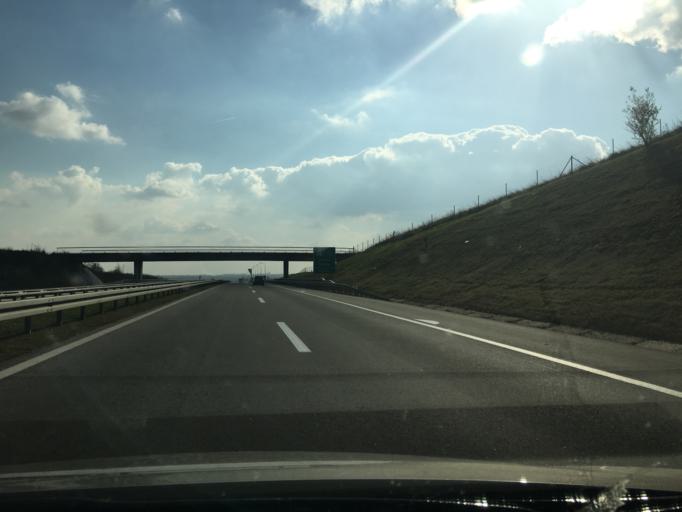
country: RS
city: Beska
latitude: 45.1555
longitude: 20.0820
